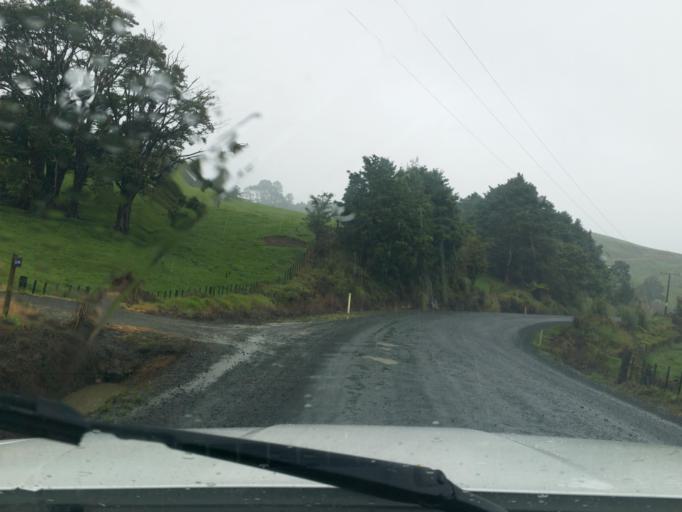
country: NZ
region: Northland
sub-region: Kaipara District
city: Dargaville
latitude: -35.8304
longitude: 174.0070
